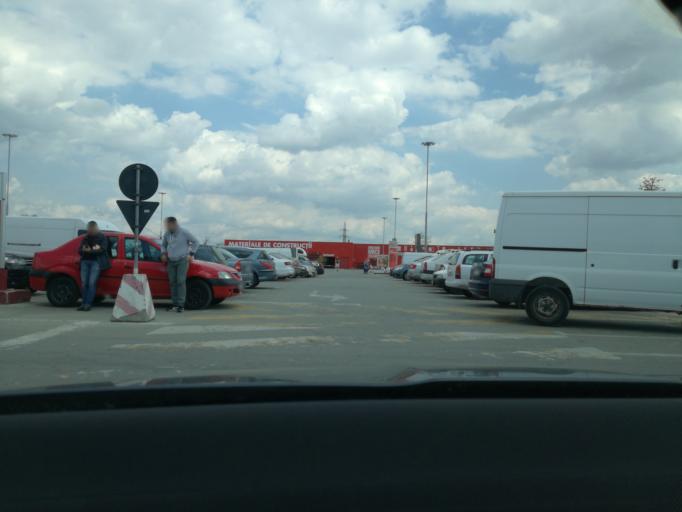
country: RO
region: Ilfov
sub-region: Comuna Chiajna
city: Chiajna
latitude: 44.4393
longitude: 25.9576
